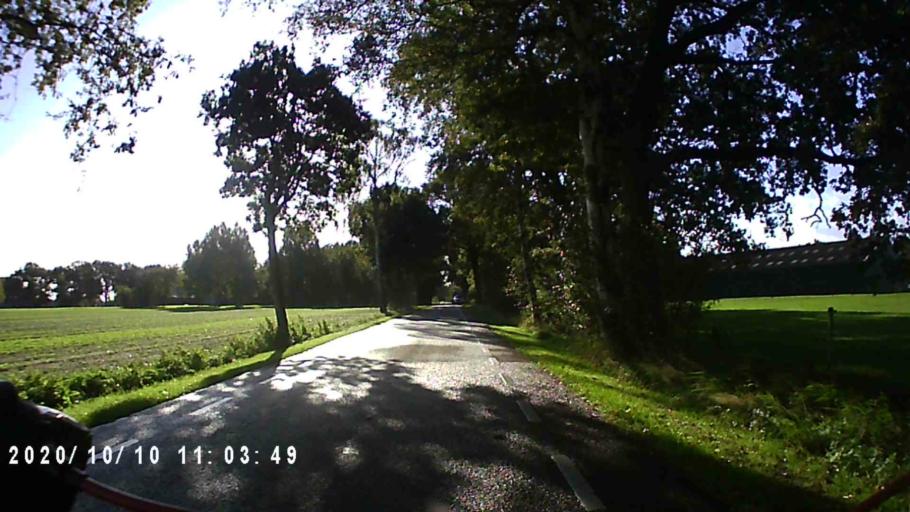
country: NL
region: Friesland
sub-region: Gemeente Achtkarspelen
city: Surhuisterveen
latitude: 53.1332
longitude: 6.2238
